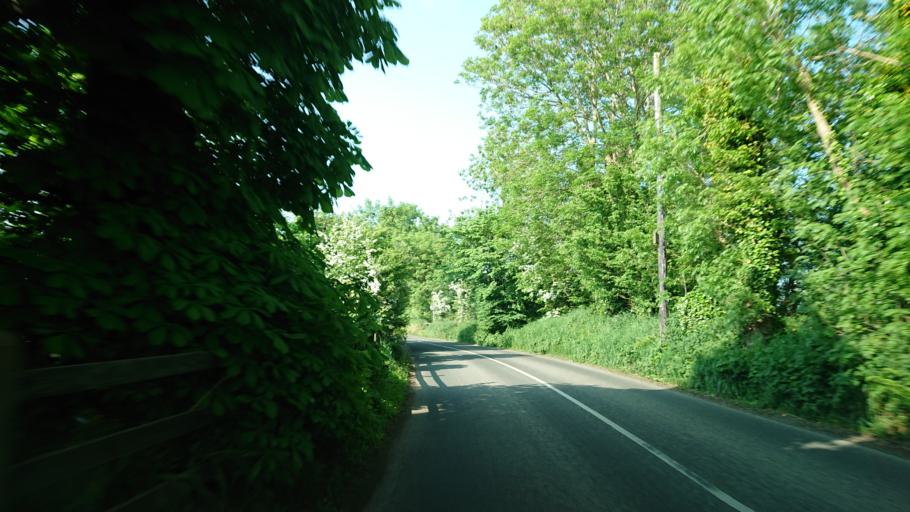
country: IE
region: Munster
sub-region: Waterford
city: Waterford
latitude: 52.2226
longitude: -7.0657
